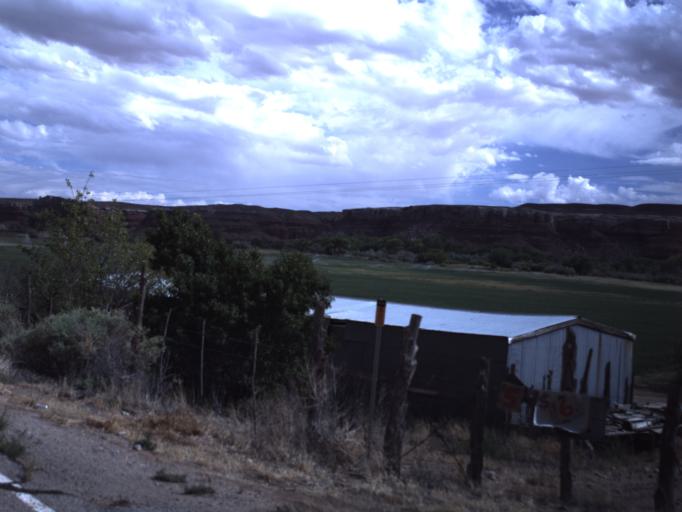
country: US
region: Utah
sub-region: San Juan County
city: Blanding
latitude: 37.2845
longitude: -109.5404
